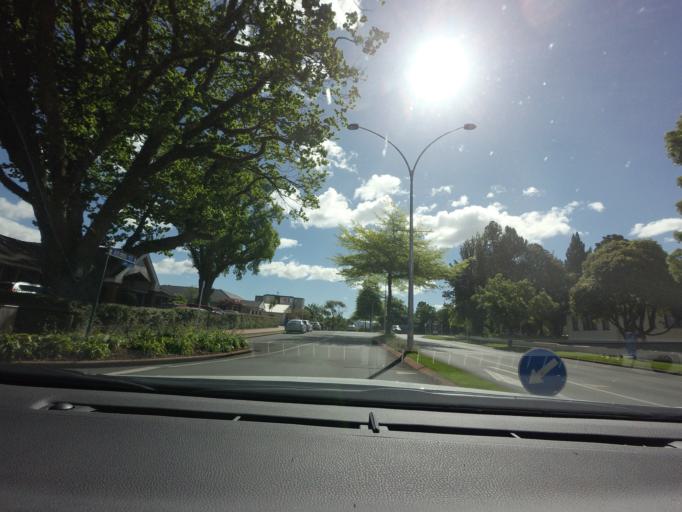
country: NZ
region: Bay of Plenty
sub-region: Rotorua District
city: Rotorua
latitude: -38.1349
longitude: 176.2488
